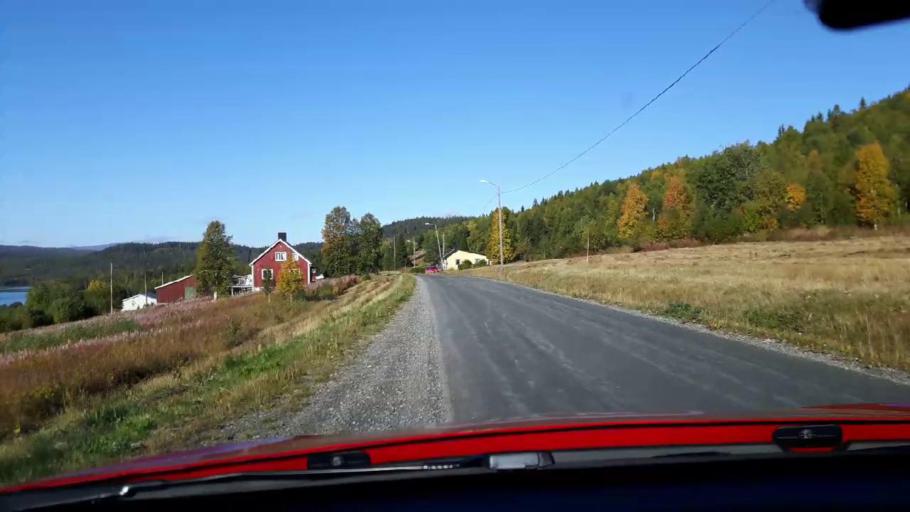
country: NO
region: Nord-Trondelag
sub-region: Lierne
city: Sandvika
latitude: 64.6072
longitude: 13.7758
